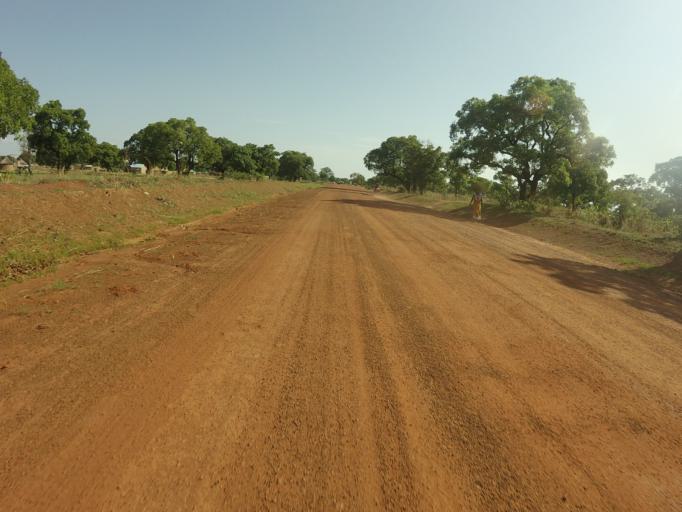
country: GH
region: Upper East
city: Bawku
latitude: 10.7827
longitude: -0.1884
